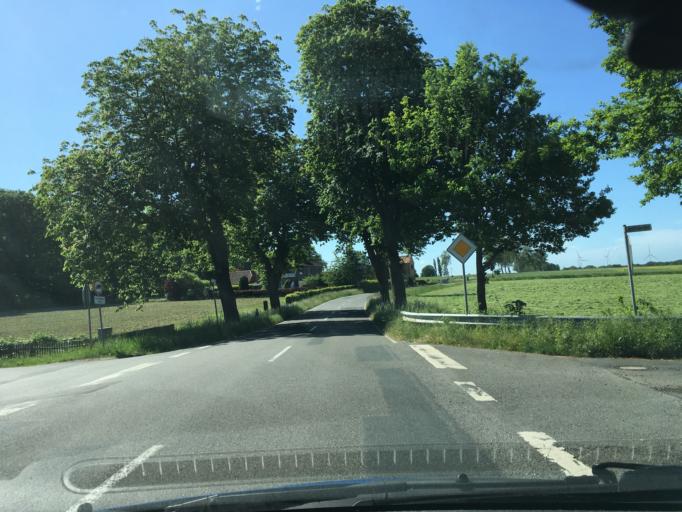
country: DE
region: Lower Saxony
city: Ebstorf
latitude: 53.0165
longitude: 10.4200
